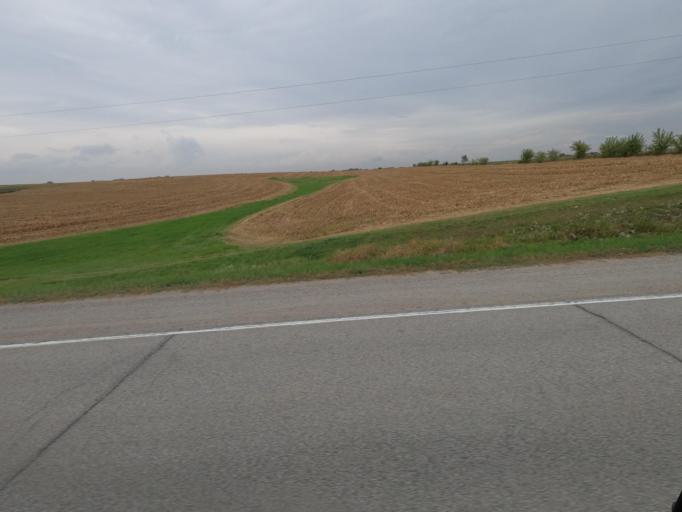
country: US
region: Iowa
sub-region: Van Buren County
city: Keosauqua
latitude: 40.8567
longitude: -92.0696
